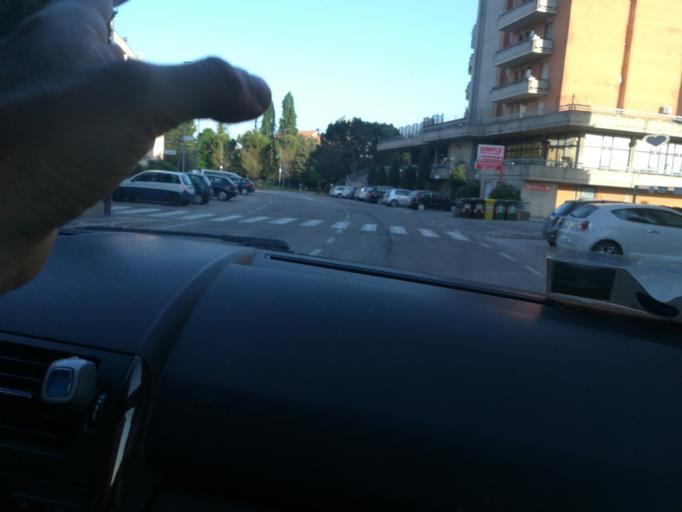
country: IT
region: The Marches
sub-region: Provincia di Macerata
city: Macerata
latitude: 43.2914
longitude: 13.4332
